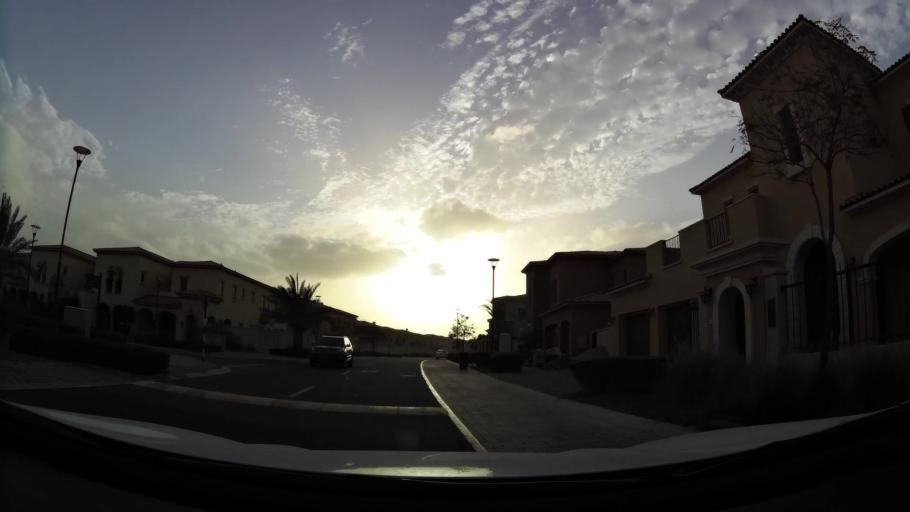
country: AE
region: Abu Dhabi
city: Abu Dhabi
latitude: 24.5349
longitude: 54.4321
